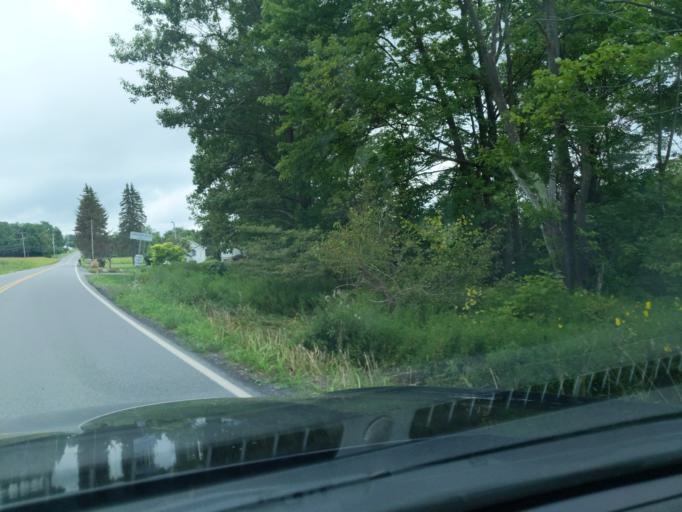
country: US
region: Pennsylvania
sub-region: Blair County
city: Claysburg
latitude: 40.3466
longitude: -78.5538
